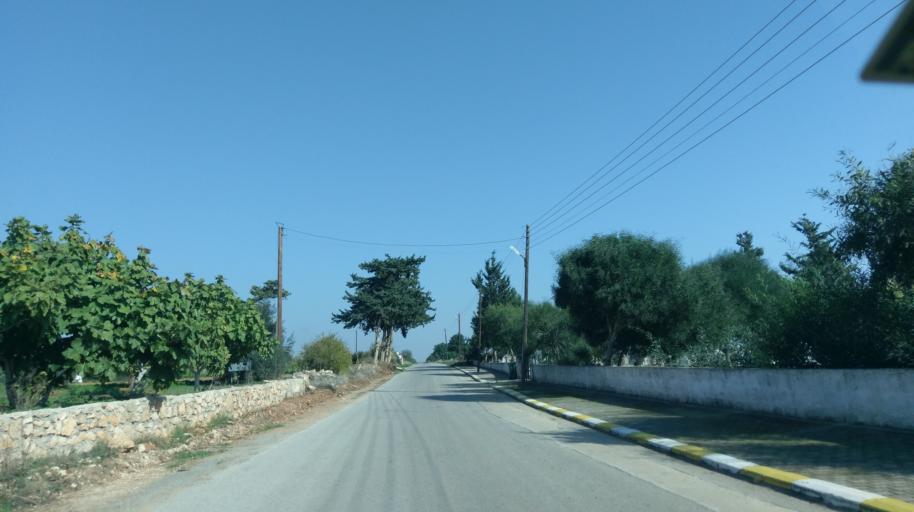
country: CY
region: Ammochostos
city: Leonarisso
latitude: 35.4836
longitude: 34.1948
